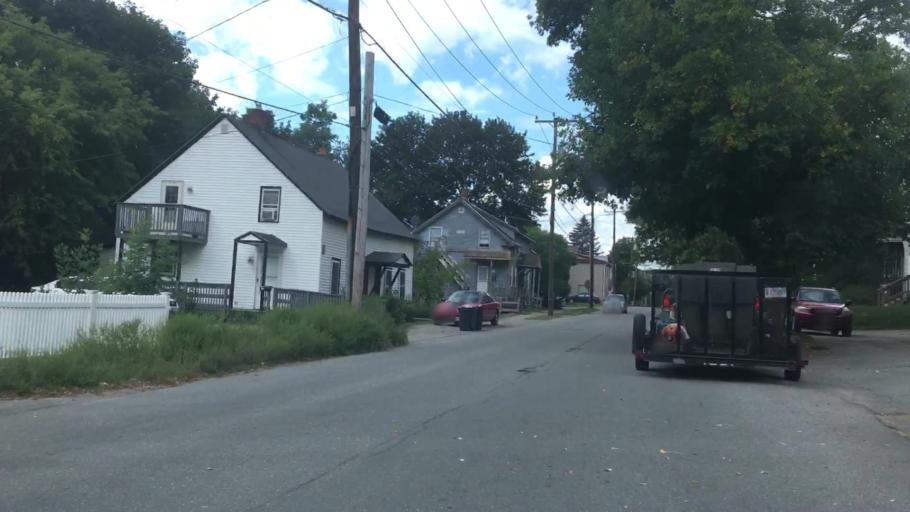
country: US
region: Maine
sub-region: Penobscot County
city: Bangor
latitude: 44.8099
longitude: -68.7724
